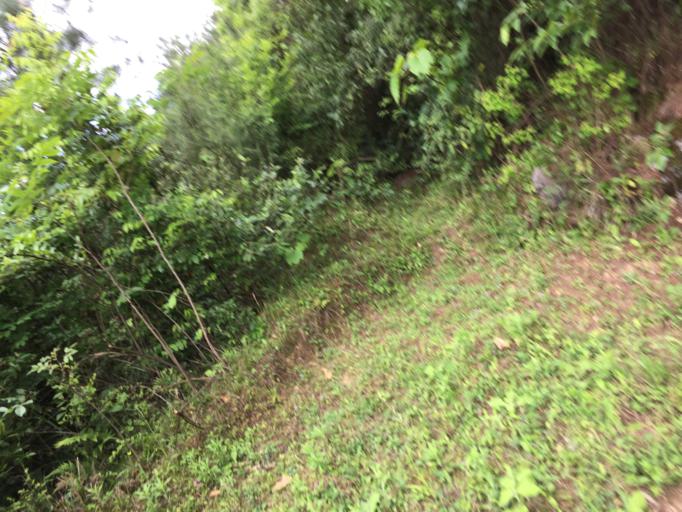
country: CN
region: Guizhou Sheng
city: Xujiaba
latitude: 27.6787
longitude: 108.0867
